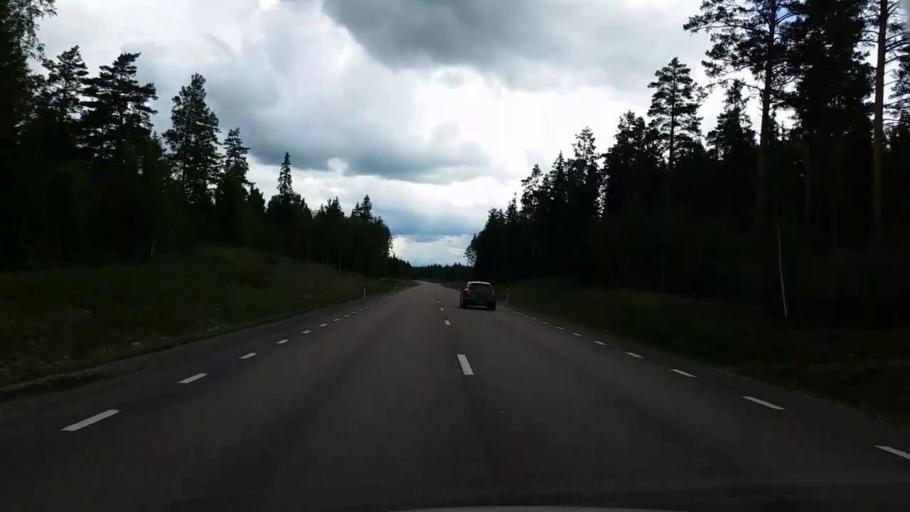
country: SE
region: Dalarna
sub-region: Avesta Kommun
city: Horndal
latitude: 60.4606
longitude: 16.4464
